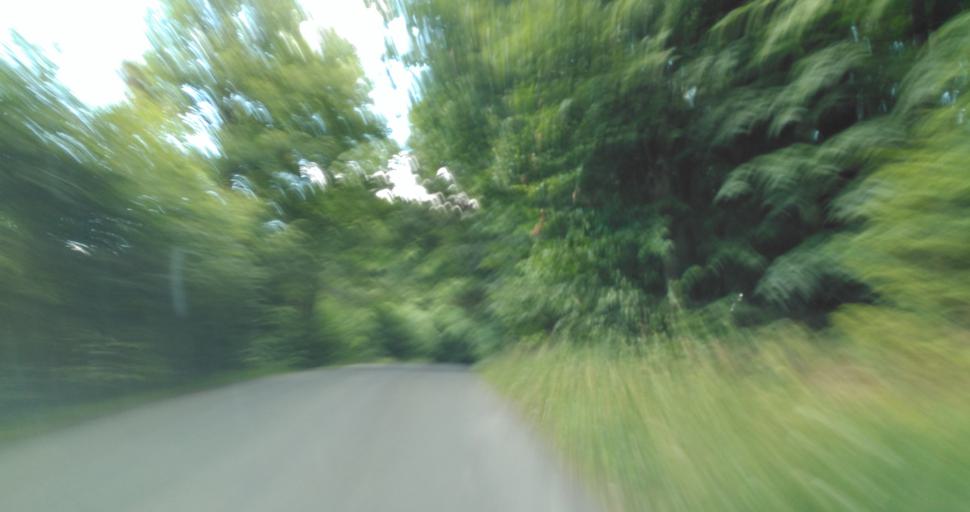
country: CZ
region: Plzensky
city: Zbiroh
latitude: 49.9214
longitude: 13.8272
